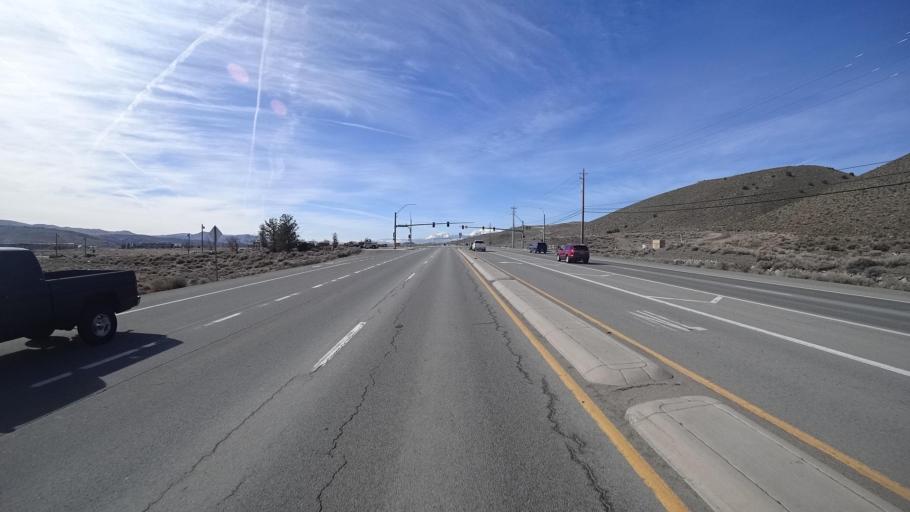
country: US
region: Nevada
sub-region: Washoe County
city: Spanish Springs
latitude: 39.6172
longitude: -119.7280
